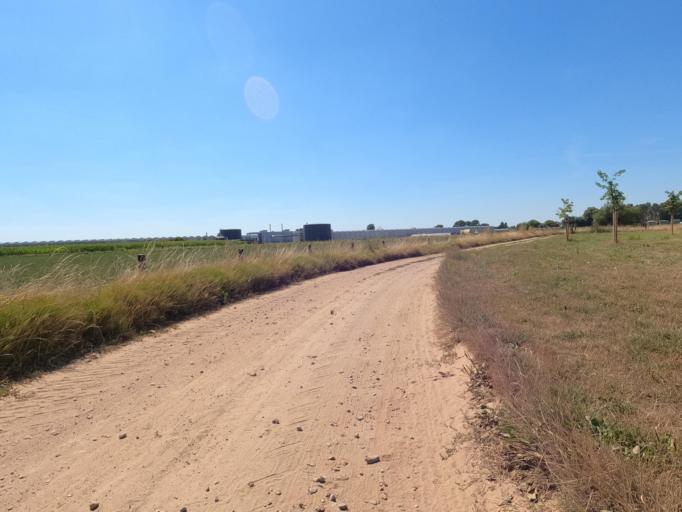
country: BE
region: Flanders
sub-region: Provincie Antwerpen
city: Wommelgem
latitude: 51.1892
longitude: 4.5242
